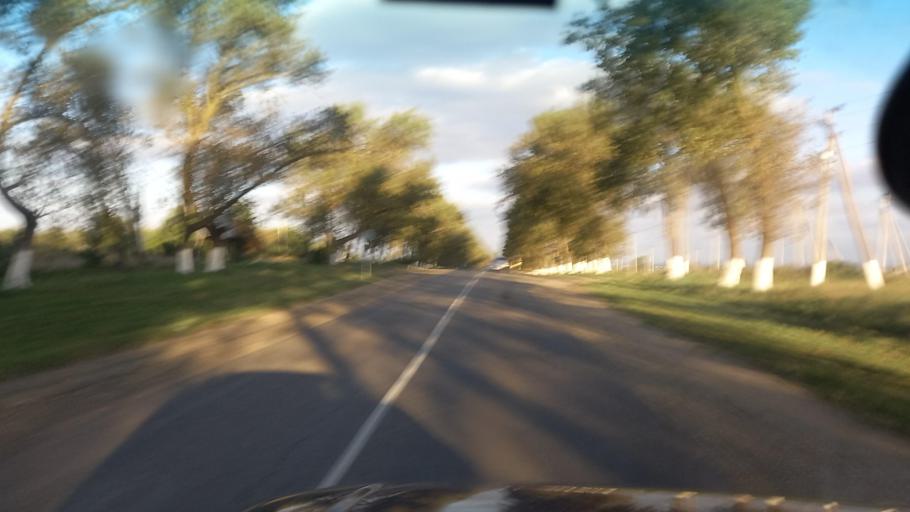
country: RU
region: Krasnodarskiy
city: Krymsk
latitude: 44.9398
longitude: 37.9320
